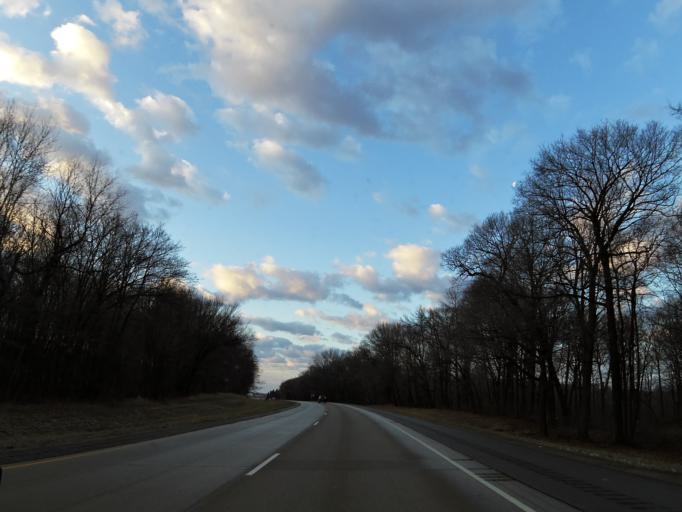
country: US
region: Minnesota
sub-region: Rice County
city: Faribault
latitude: 44.3780
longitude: -93.2956
